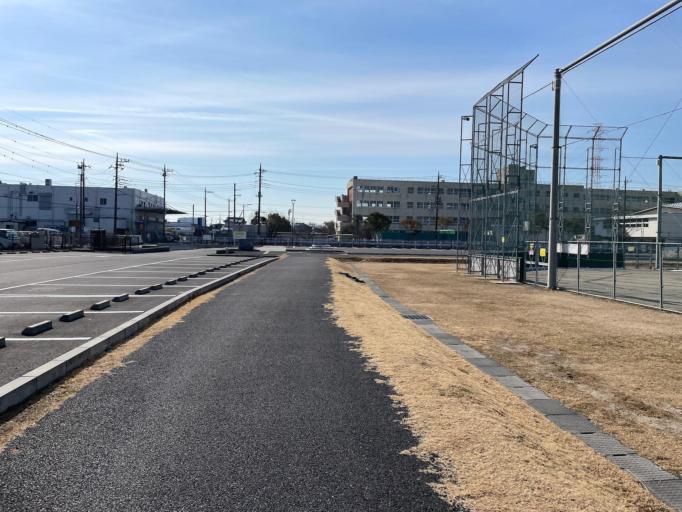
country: JP
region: Chiba
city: Nagareyama
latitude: 35.8589
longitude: 139.8760
